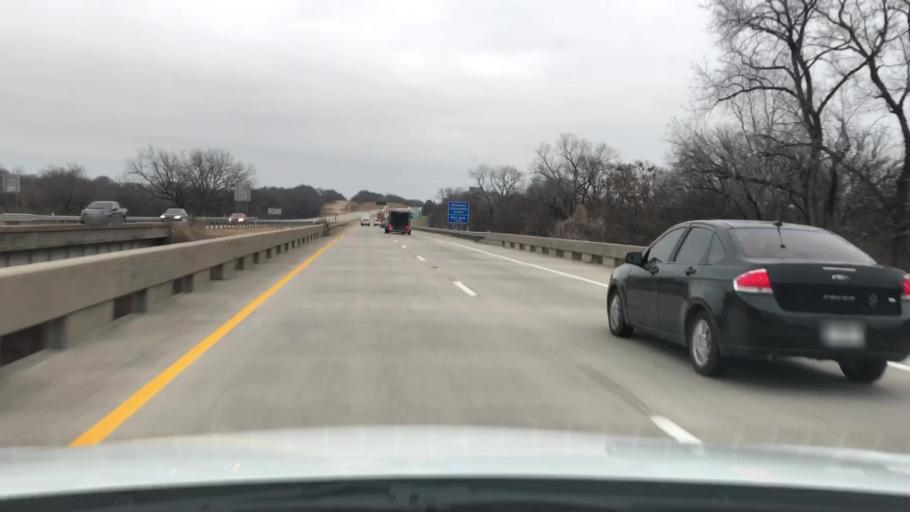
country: US
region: Texas
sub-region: Cooke County
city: Gainesville
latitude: 33.7288
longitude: -97.1580
